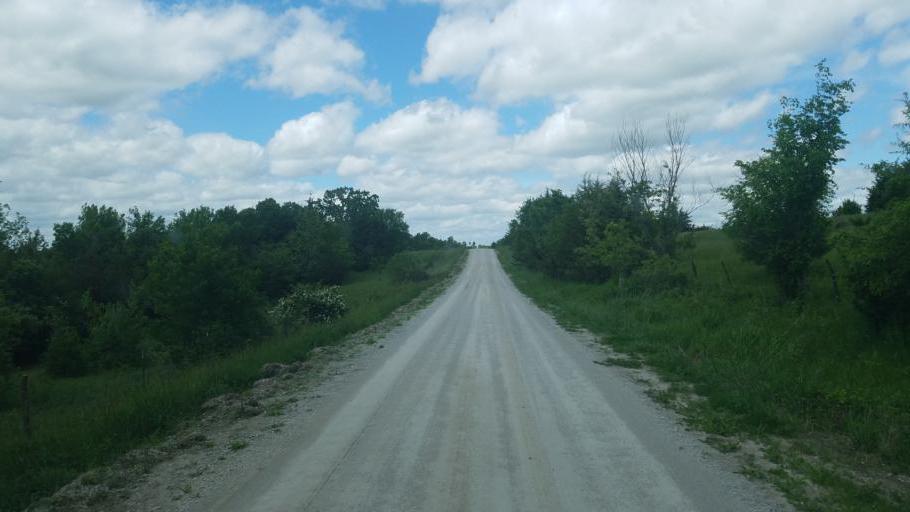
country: US
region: Iowa
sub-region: Decatur County
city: Lamoni
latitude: 40.5245
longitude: -94.0231
